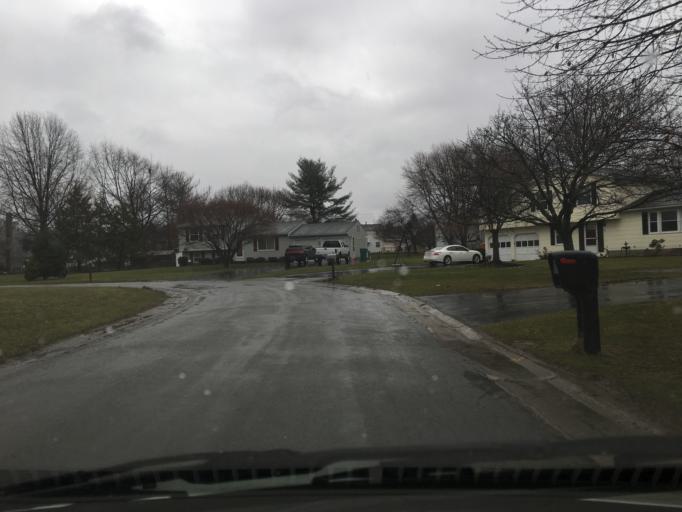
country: US
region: New York
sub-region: Monroe County
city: East Rochester
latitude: 43.1691
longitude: -77.4905
